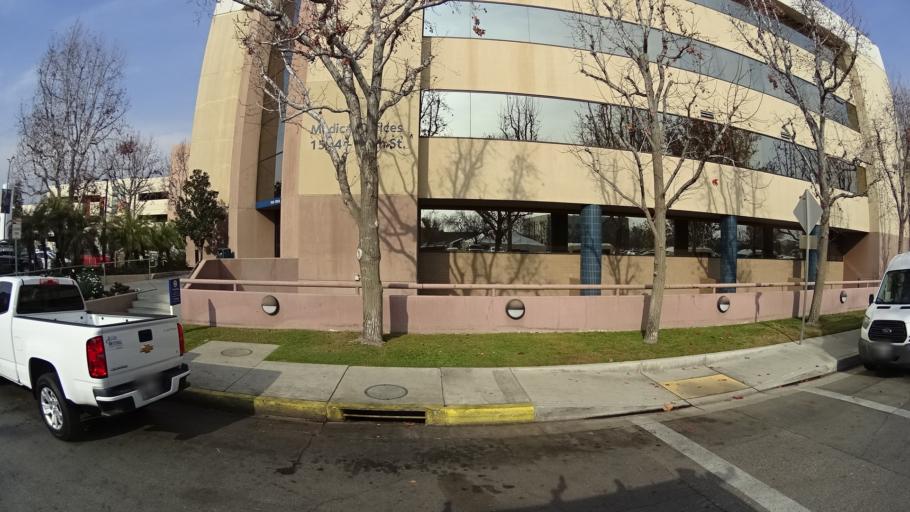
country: US
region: California
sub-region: Kern County
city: Bakersfield
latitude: 35.3839
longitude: -119.0198
